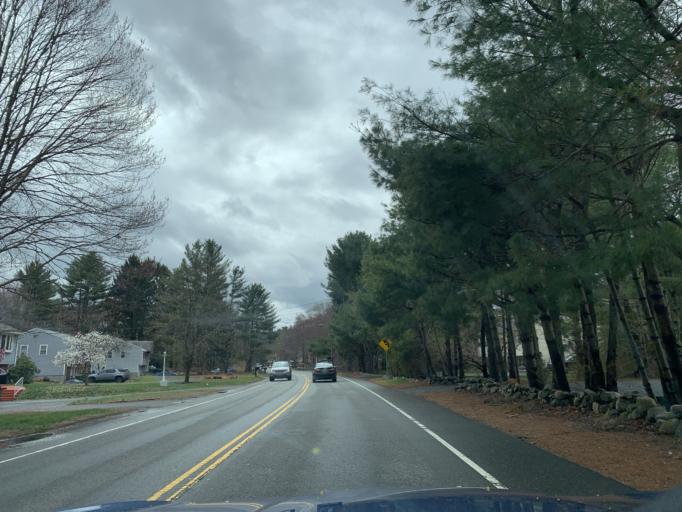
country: US
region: Massachusetts
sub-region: Bristol County
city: Mansfield Center
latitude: 42.0065
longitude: -71.2437
